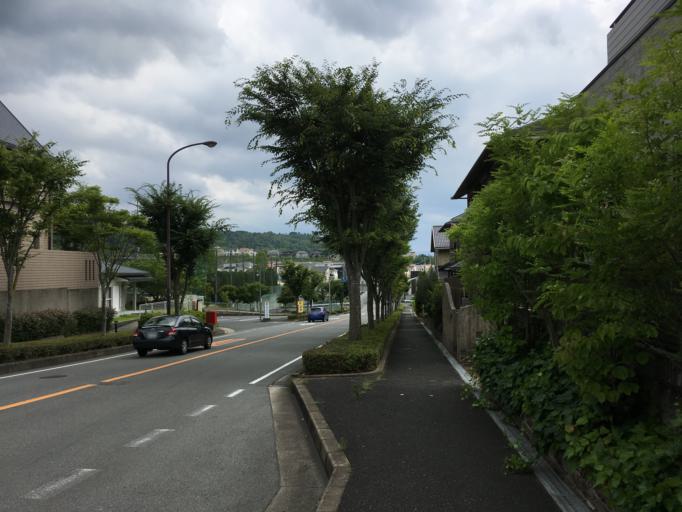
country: JP
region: Nara
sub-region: Ikoma-shi
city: Ikoma
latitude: 34.6742
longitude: 135.7187
